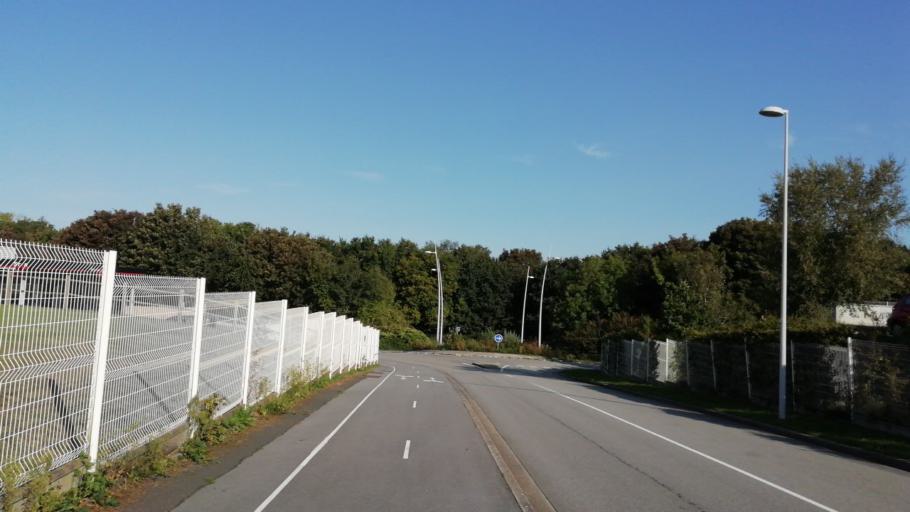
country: FR
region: Haute-Normandie
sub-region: Departement de la Seine-Maritime
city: Harfleur
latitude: 49.5155
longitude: 0.2074
